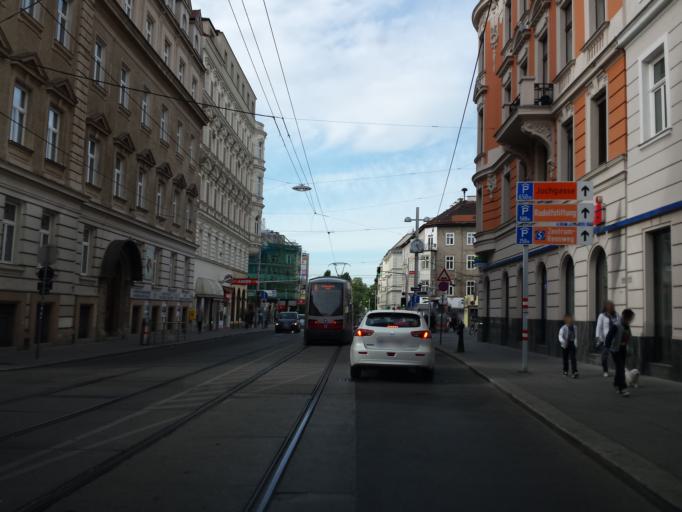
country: AT
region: Vienna
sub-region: Wien Stadt
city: Vienna
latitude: 48.1937
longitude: 16.3864
